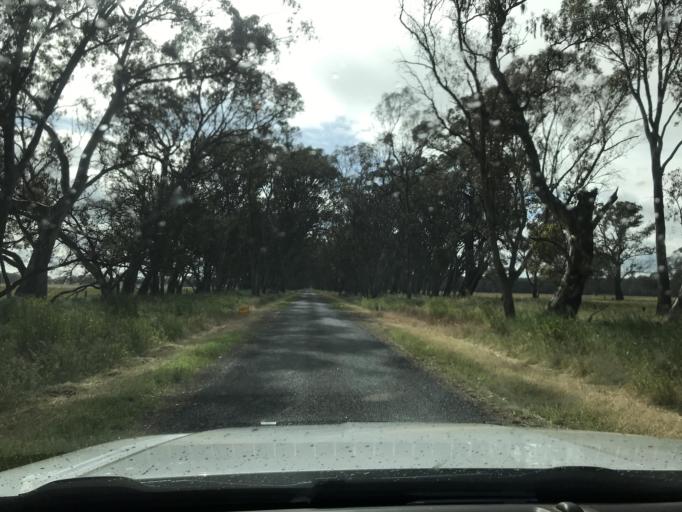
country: AU
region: South Australia
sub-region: Wattle Range
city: Penola
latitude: -37.1905
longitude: 141.2580
